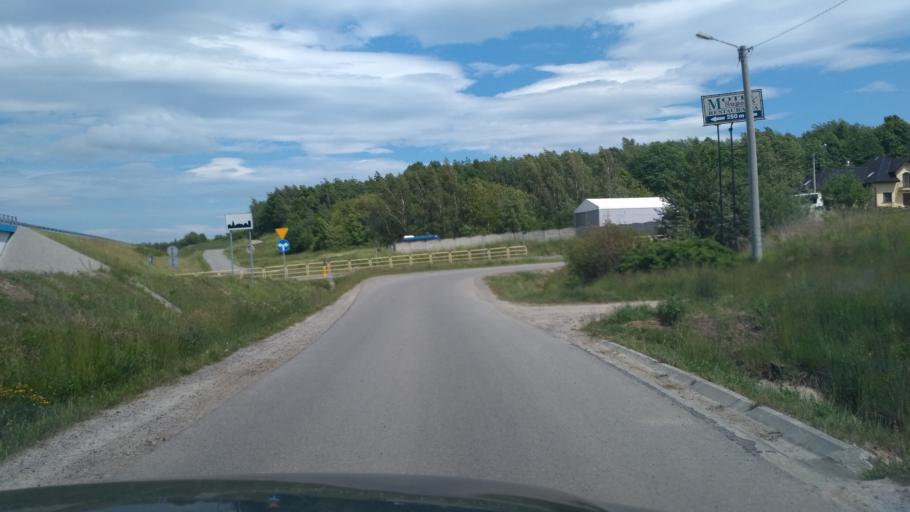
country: PL
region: Subcarpathian Voivodeship
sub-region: Powiat ropczycko-sedziszowski
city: Ropczyce
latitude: 50.0498
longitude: 21.6202
